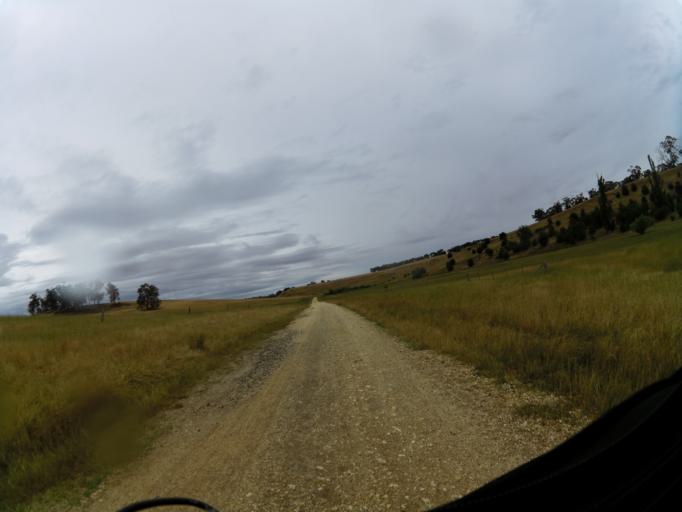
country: AU
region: Victoria
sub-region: Mount Alexander
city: Castlemaine
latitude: -37.2088
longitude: 144.0261
